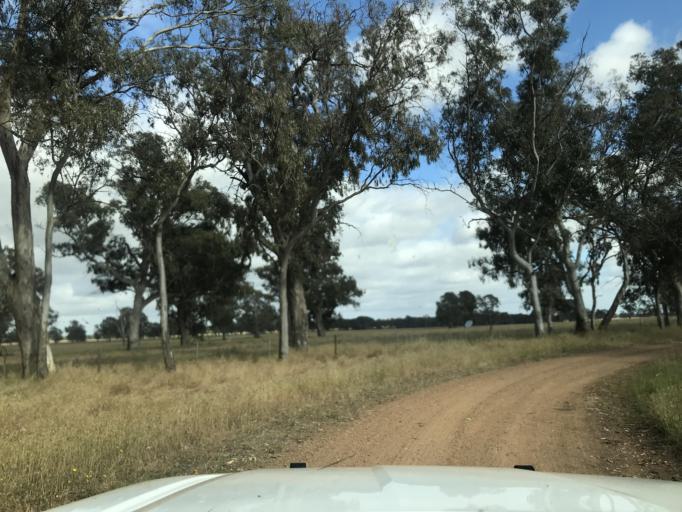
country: AU
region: South Australia
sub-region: Wattle Range
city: Penola
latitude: -37.1949
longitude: 141.0012
